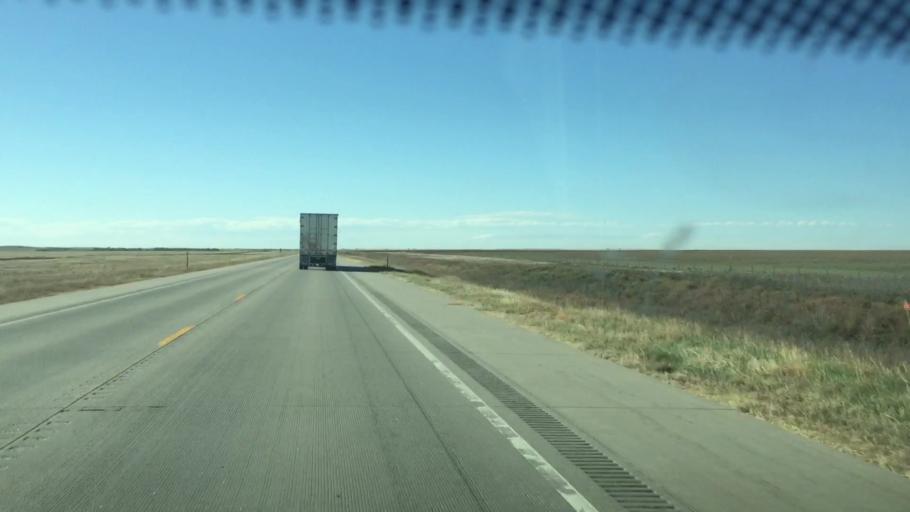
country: US
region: Colorado
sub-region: Kiowa County
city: Eads
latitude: 38.7922
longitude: -102.9379
